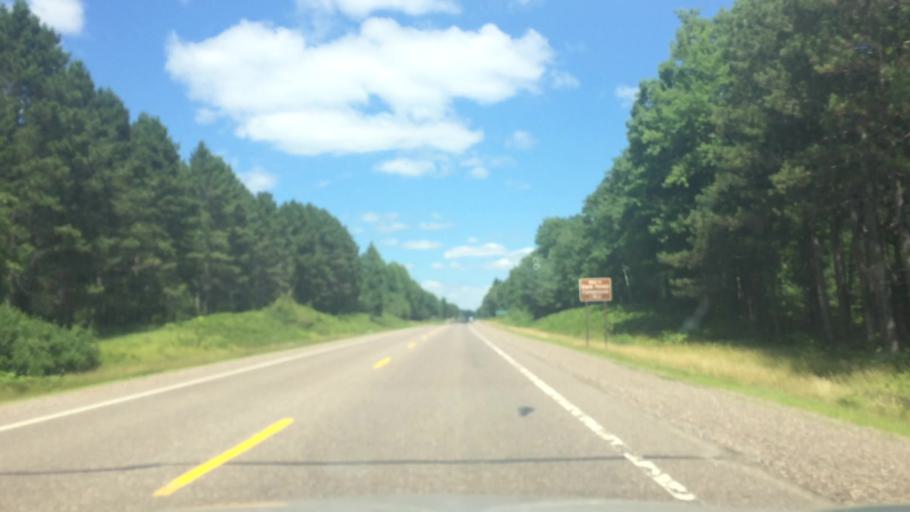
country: US
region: Wisconsin
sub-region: Vilas County
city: Lac du Flambeau
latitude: 45.9674
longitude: -89.6999
